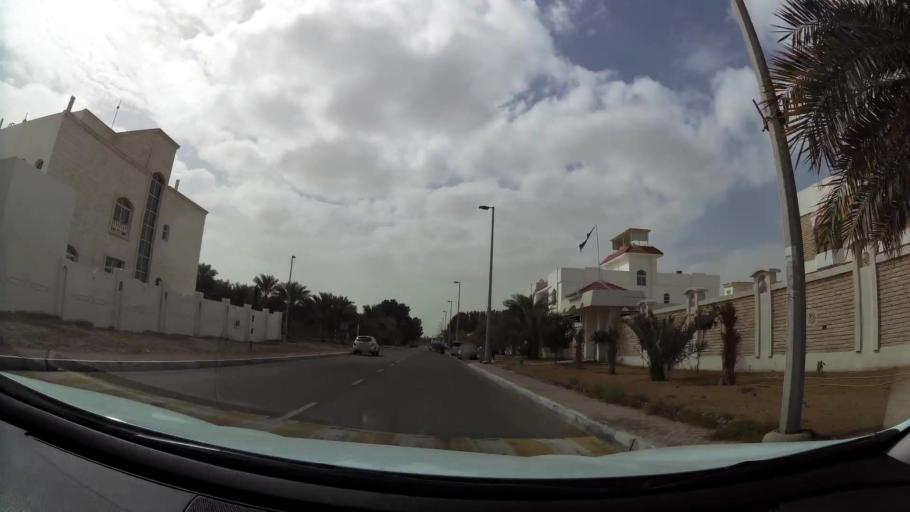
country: AE
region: Abu Dhabi
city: Abu Dhabi
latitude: 24.4018
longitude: 54.5147
